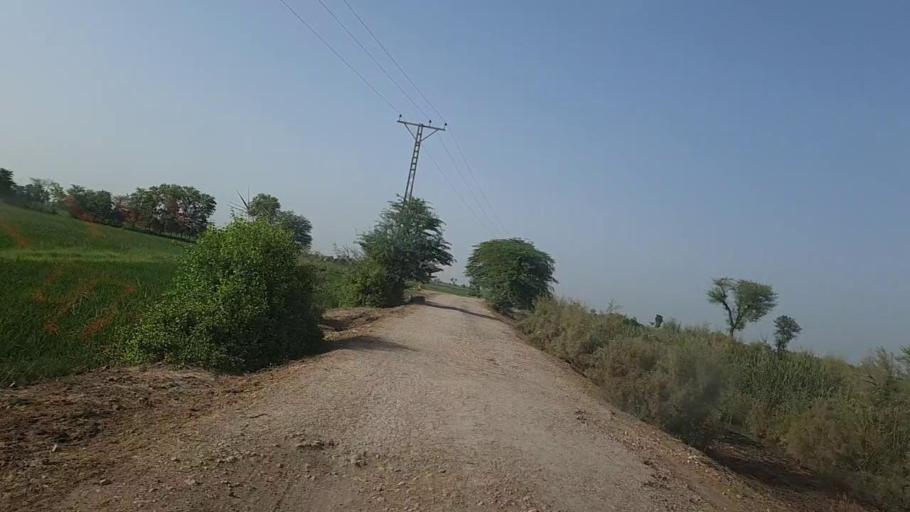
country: PK
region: Sindh
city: Sita Road
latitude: 27.1044
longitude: 67.8744
